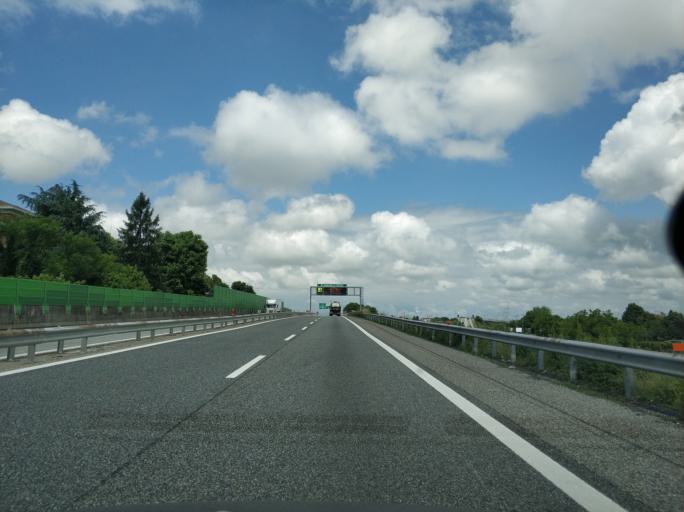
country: IT
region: Piedmont
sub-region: Provincia di Torino
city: Settimo Torinese
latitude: 45.1232
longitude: 7.7328
